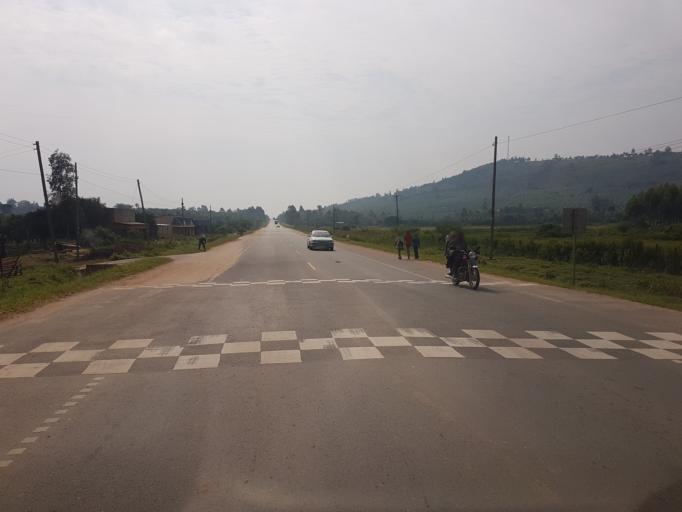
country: UG
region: Western Region
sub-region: Sheema District
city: Kibingo
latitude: -0.6416
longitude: 30.5044
